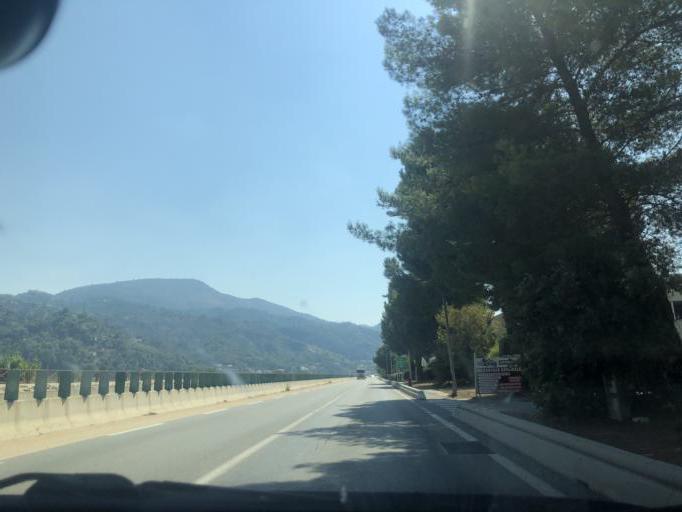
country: FR
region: Provence-Alpes-Cote d'Azur
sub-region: Departement des Alpes-Maritimes
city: Carros
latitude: 43.7924
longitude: 7.2071
